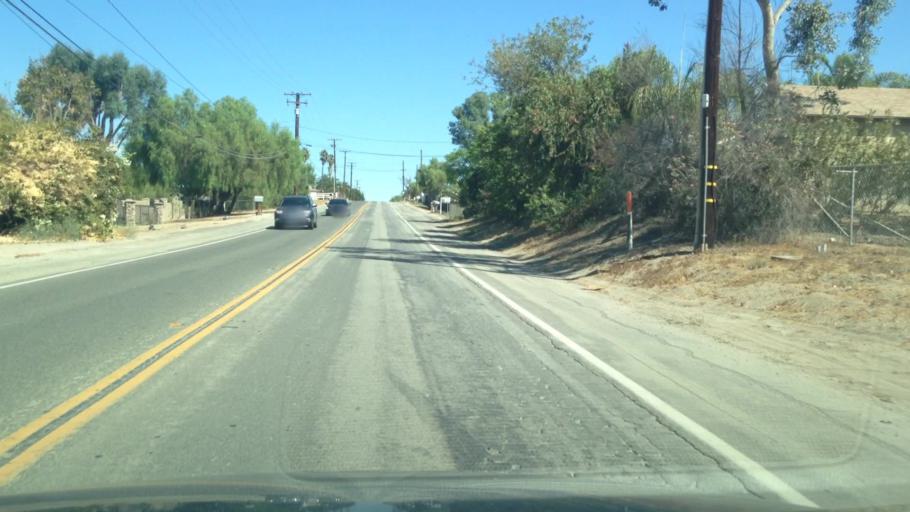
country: US
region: California
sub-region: Riverside County
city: Woodcrest
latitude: 33.8635
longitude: -117.3314
